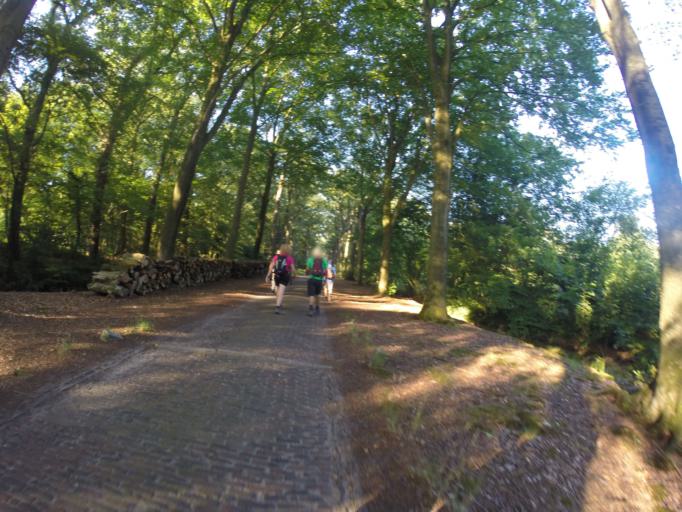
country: NL
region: Gelderland
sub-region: Gemeente Lochem
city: Barchem
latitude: 52.0965
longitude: 6.4088
